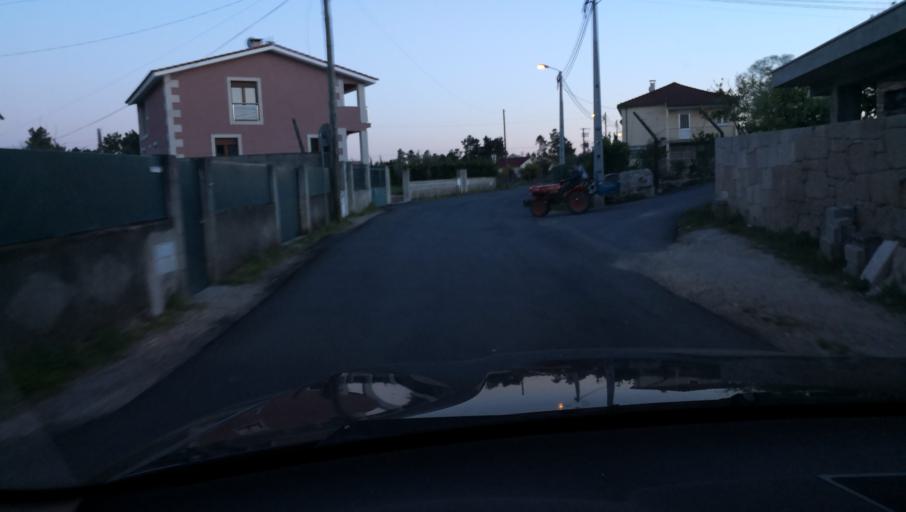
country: PT
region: Vila Real
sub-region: Vila Real
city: Vila Real
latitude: 41.2897
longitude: -7.6804
